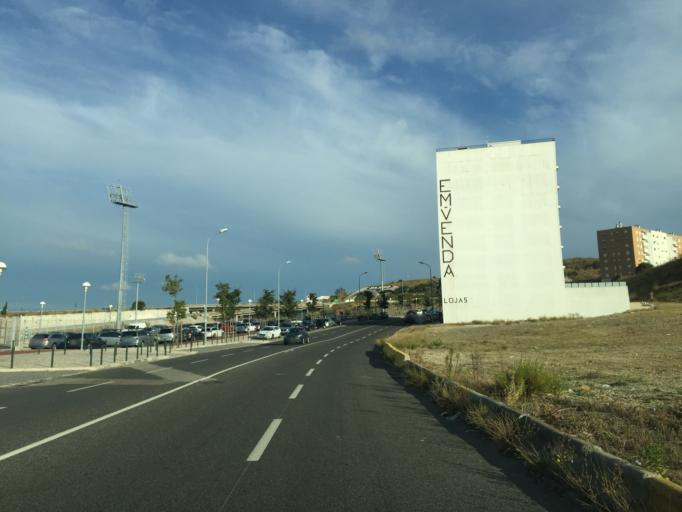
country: PT
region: Lisbon
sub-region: Odivelas
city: Olival do Basto
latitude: 38.7812
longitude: -9.1528
